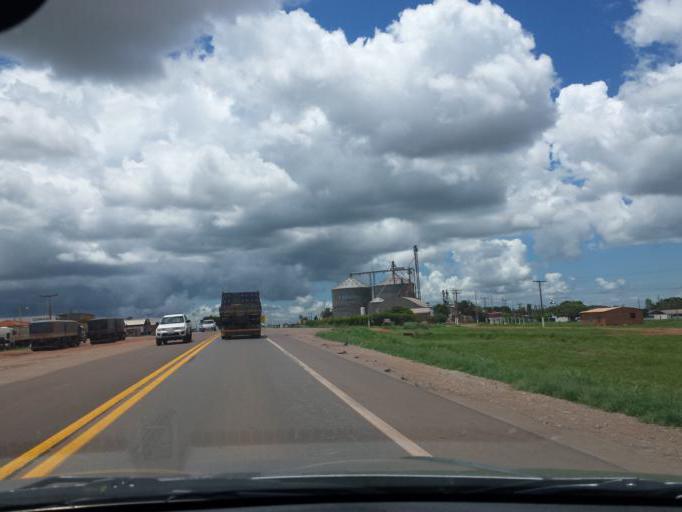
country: BR
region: Goias
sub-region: Cristalina
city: Cristalina
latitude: -16.7747
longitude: -47.6230
